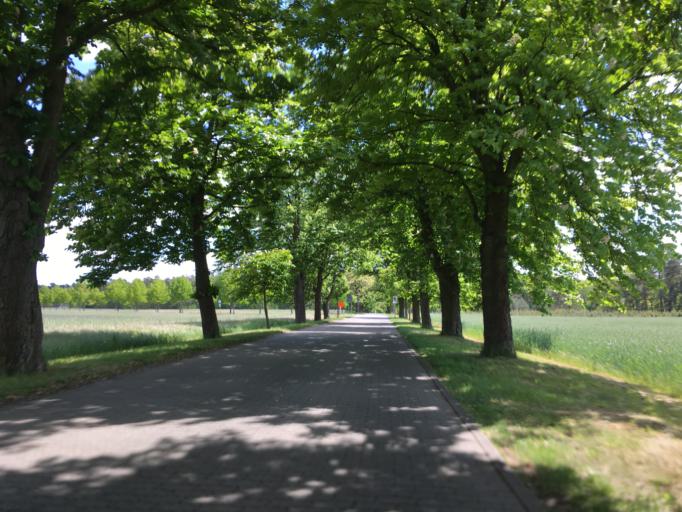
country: DE
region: Brandenburg
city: Biesenthal
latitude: 52.7507
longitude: 13.6479
